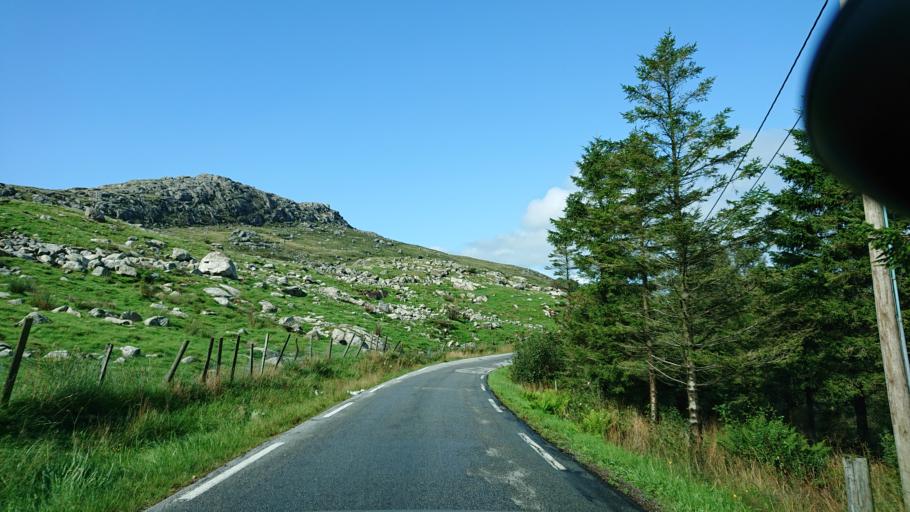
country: NO
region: Rogaland
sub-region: Gjesdal
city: Algard
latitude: 58.6981
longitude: 5.8893
